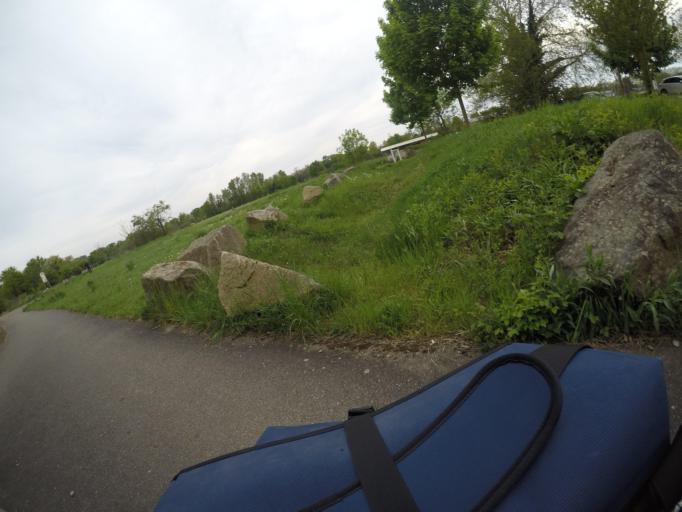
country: FR
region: Alsace
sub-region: Departement du Bas-Rhin
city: Eschau
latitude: 48.5093
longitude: 7.7352
